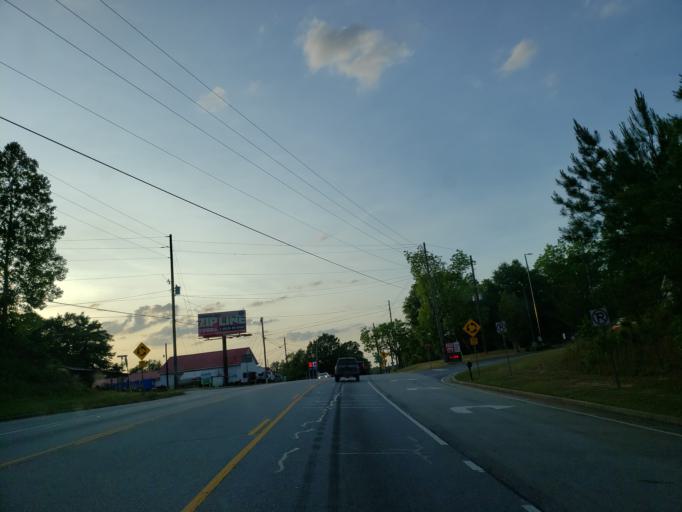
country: US
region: Georgia
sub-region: Coweta County
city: Newnan
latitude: 33.4902
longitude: -84.9114
